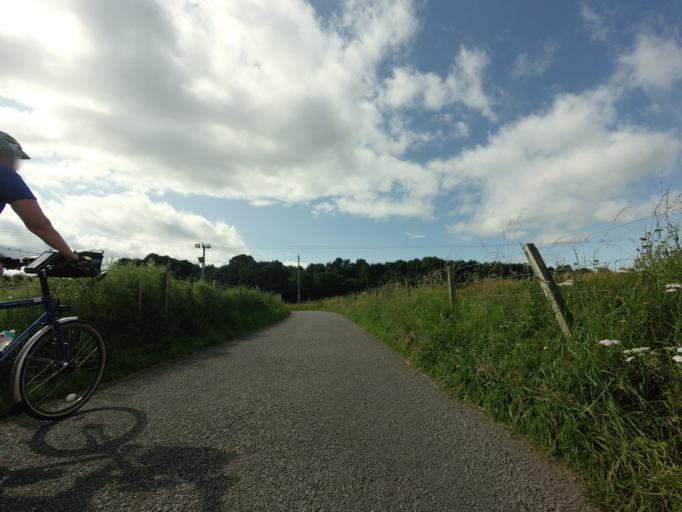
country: GB
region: Scotland
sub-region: Highland
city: Nairn
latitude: 57.5698
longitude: -3.8679
